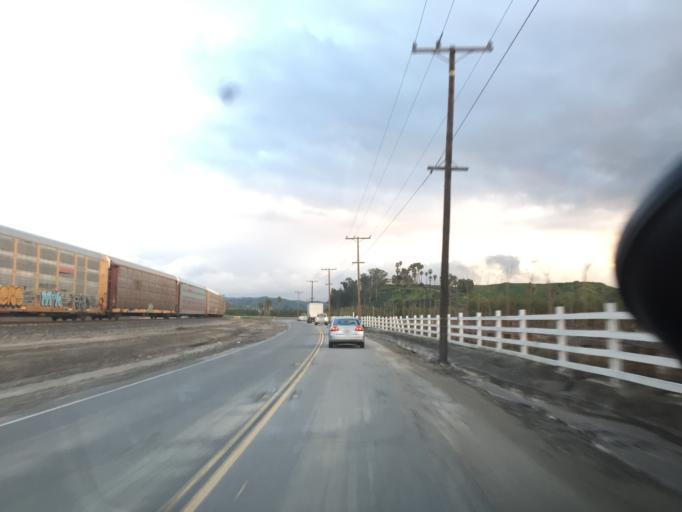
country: US
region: California
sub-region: San Bernardino County
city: Redlands
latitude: 34.0250
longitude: -117.2007
